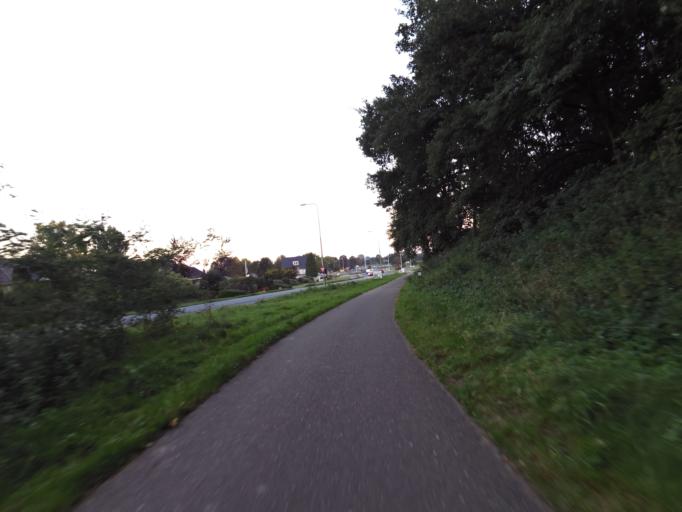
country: NL
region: Gelderland
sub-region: Gemeente Montferland
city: s-Heerenberg
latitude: 51.8982
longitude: 6.2553
